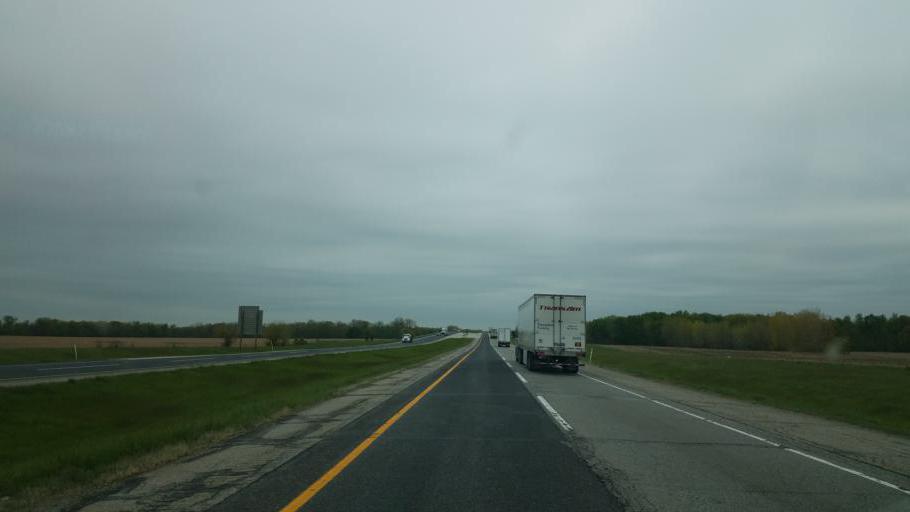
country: US
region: Michigan
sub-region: Saint Joseph County
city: Sturgis
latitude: 41.7537
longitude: -85.4397
